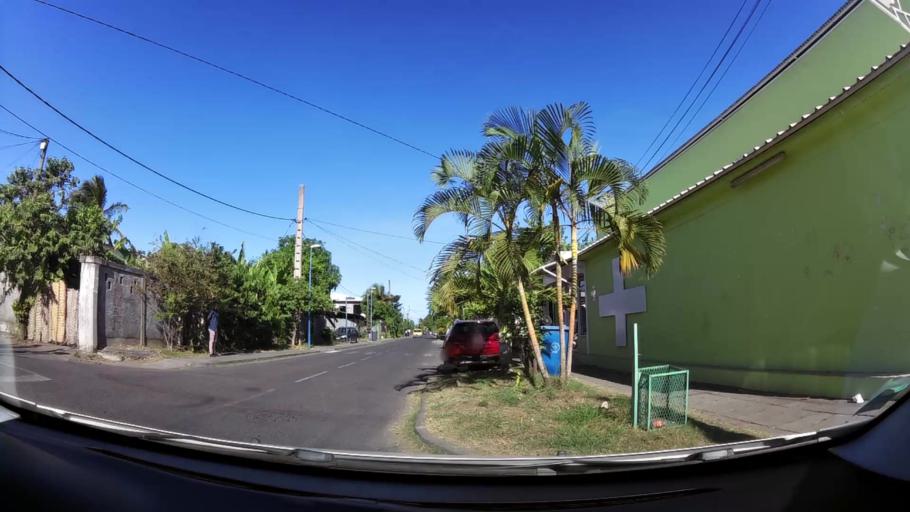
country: YT
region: Pamandzi
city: Pamandzi
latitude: -12.7990
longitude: 45.2770
